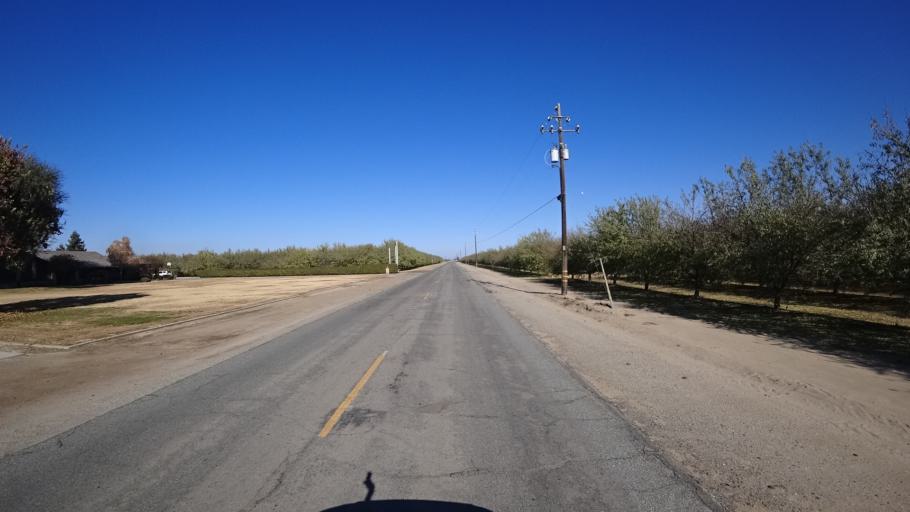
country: US
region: California
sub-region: Kern County
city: Greenfield
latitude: 35.2482
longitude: -119.0567
